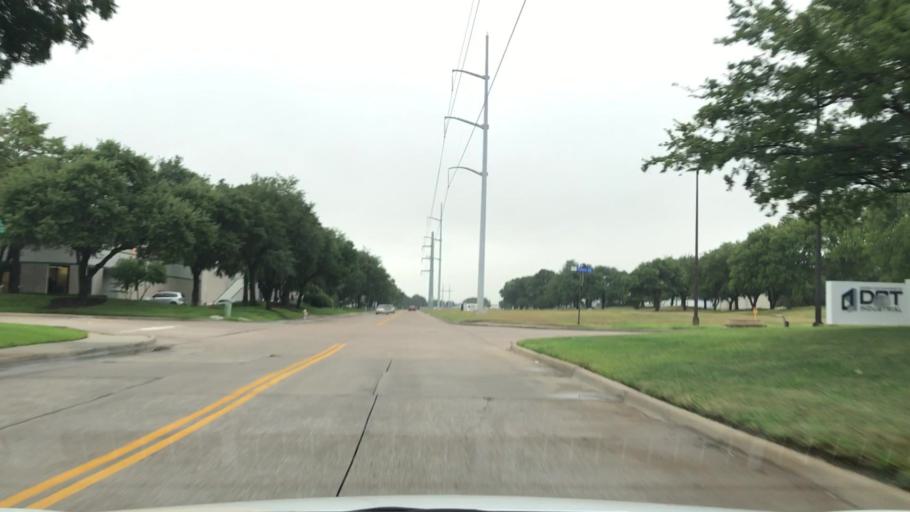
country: US
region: Texas
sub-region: Dallas County
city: Coppell
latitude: 32.9309
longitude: -97.0199
